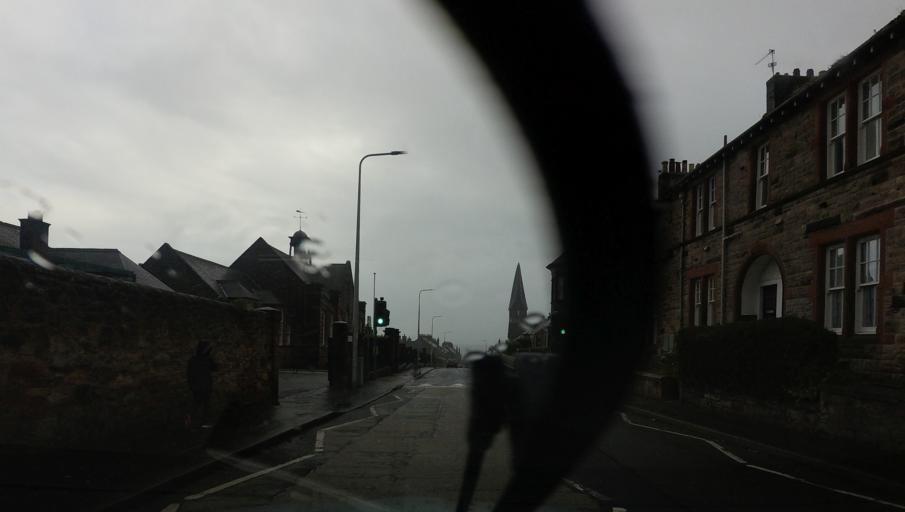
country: GB
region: Scotland
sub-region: Fife
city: Kirkcaldy
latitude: 56.1296
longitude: -3.1219
